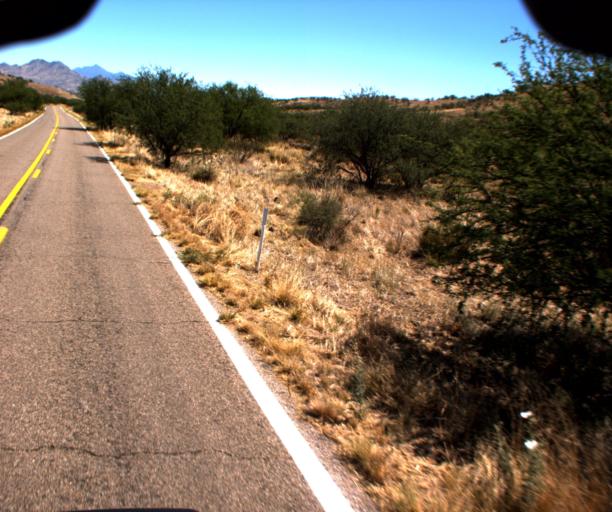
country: US
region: Arizona
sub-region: Santa Cruz County
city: Rio Rico
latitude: 31.4053
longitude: -111.0252
